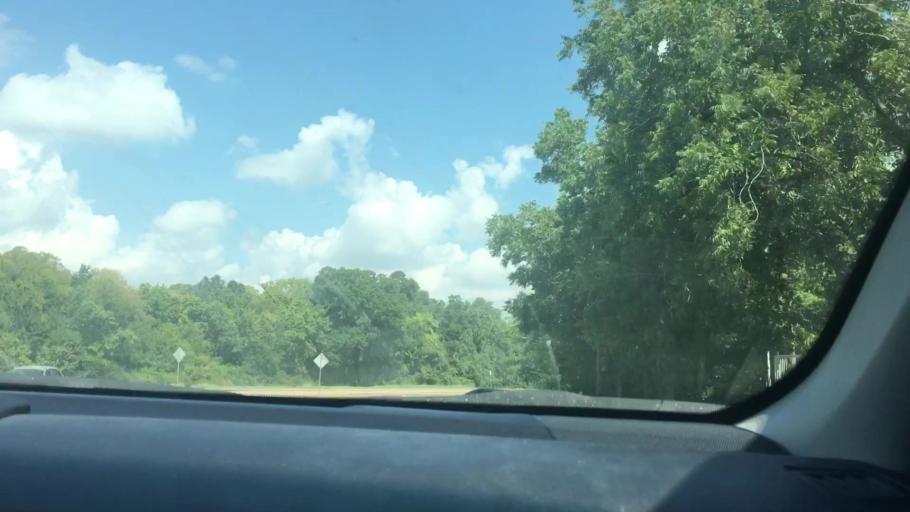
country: US
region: Texas
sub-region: Fort Bend County
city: Fifth Street
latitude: 29.5943
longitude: -95.5609
